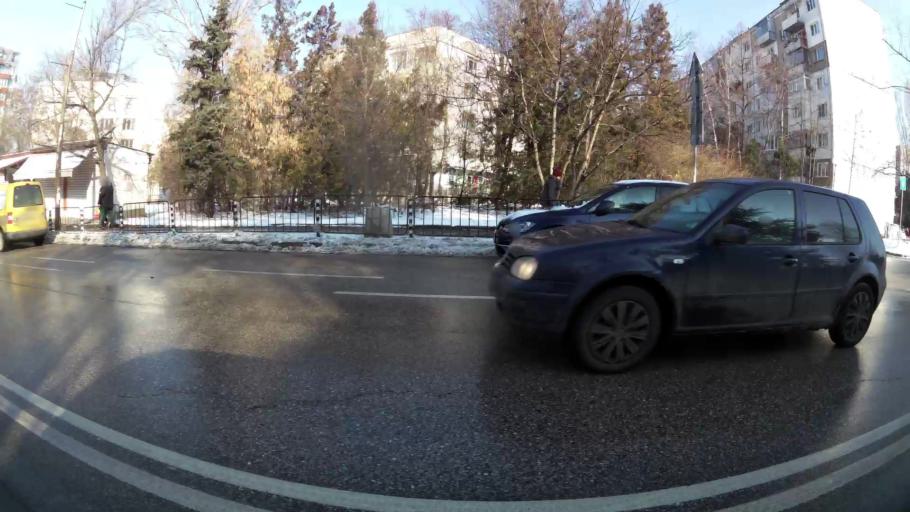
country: BG
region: Sofia-Capital
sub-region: Stolichna Obshtina
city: Sofia
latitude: 42.6620
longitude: 23.3458
